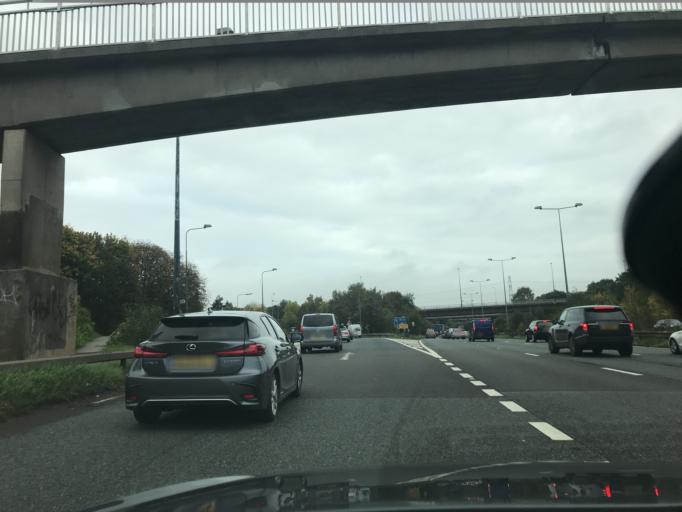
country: GB
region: England
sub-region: Manchester
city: Chorlton cum Hardy
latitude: 53.4108
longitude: -2.2667
